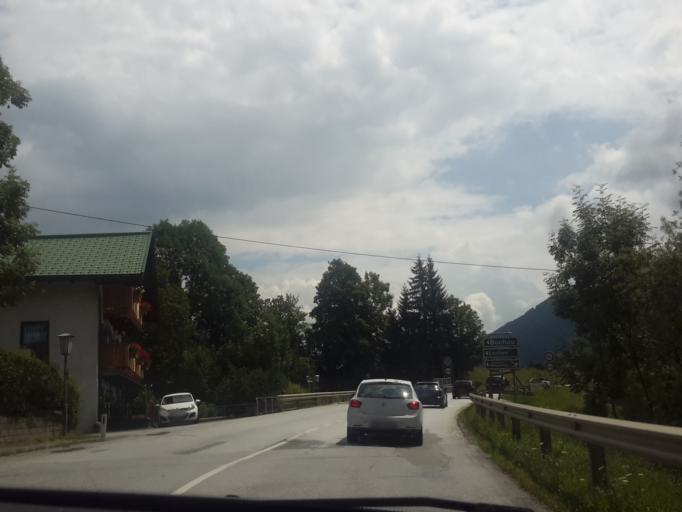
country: AT
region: Tyrol
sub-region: Politischer Bezirk Kufstein
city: Ellmau
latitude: 47.5220
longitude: 12.2829
